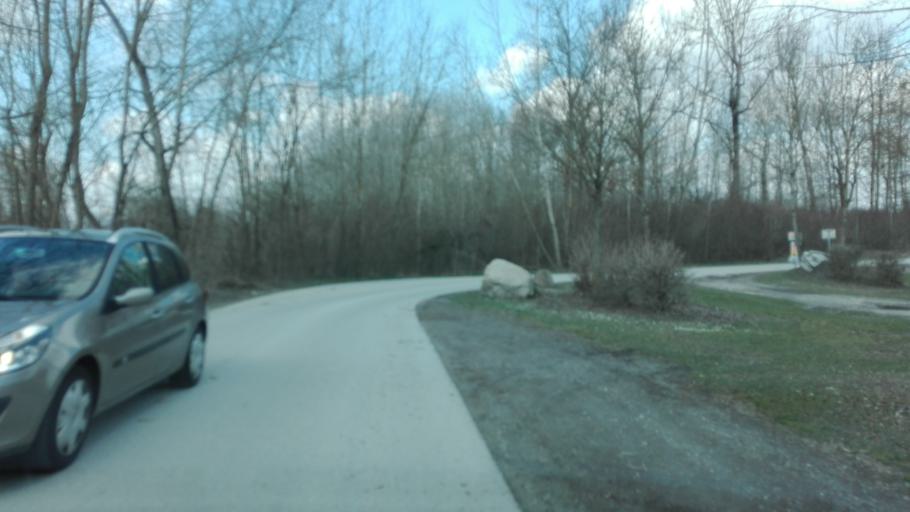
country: AT
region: Upper Austria
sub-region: Politischer Bezirk Urfahr-Umgebung
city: Feldkirchen an der Donau
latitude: 48.3247
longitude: 14.0612
